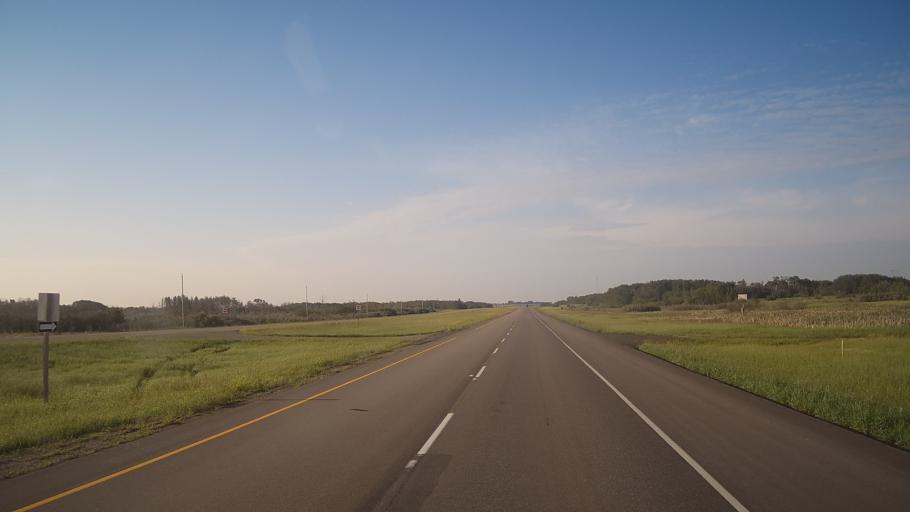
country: CA
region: Saskatchewan
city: Saskatoon
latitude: 51.8825
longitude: -106.5132
